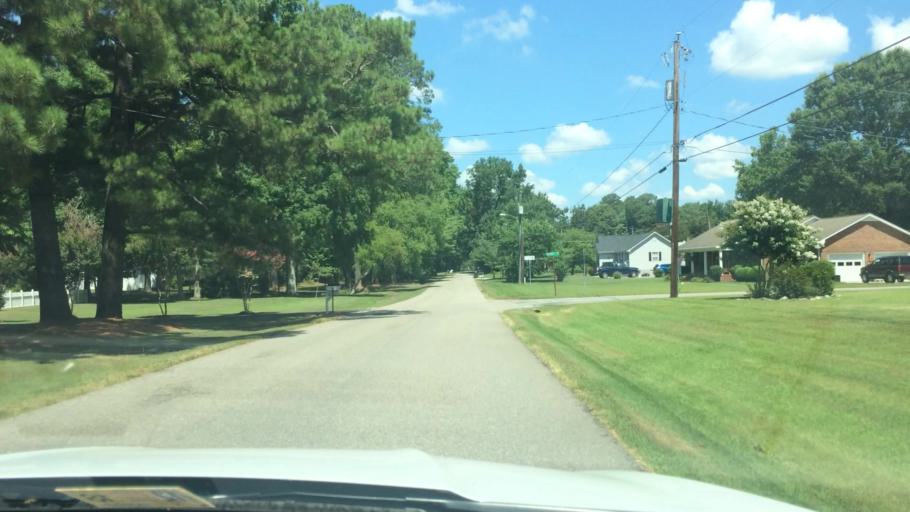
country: US
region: Virginia
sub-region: King William County
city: West Point
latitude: 37.5677
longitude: -76.8041
